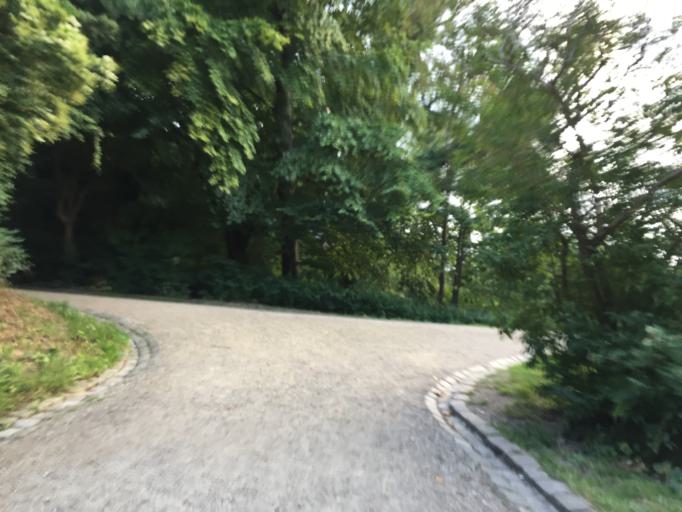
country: DK
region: Capital Region
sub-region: Kobenhavn
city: Copenhagen
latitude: 55.6895
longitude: 12.5805
